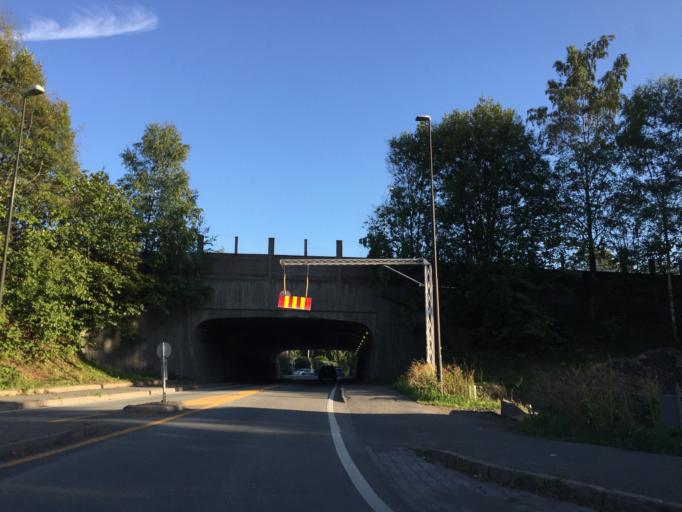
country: NO
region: Akershus
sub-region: Baerum
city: Lysaker
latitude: 59.9038
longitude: 10.5967
